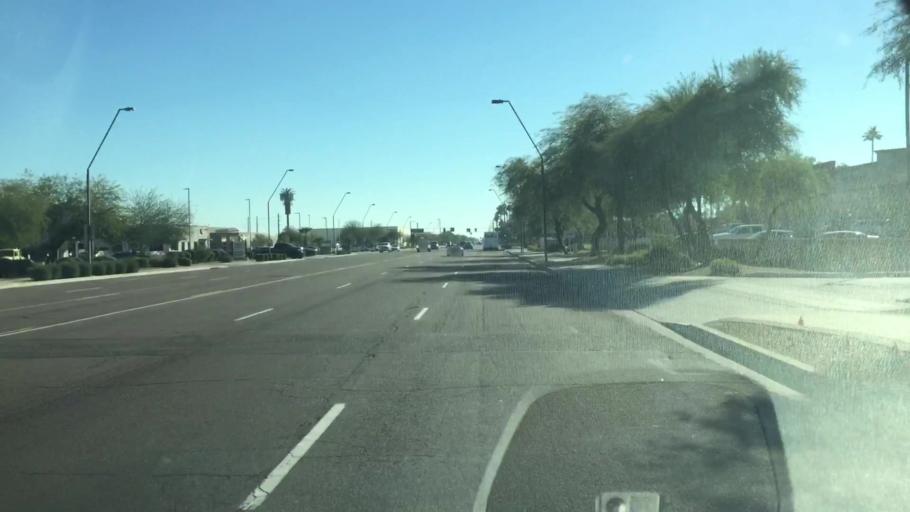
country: US
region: Arizona
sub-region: Maricopa County
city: Guadalupe
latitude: 33.3431
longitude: -111.9632
